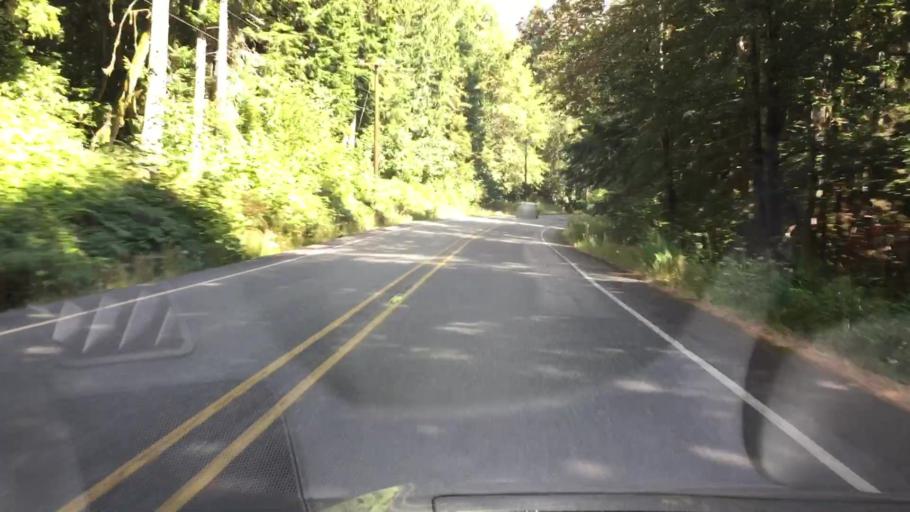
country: US
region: Washington
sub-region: Pierce County
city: Eatonville
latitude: 46.7557
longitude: -121.9695
